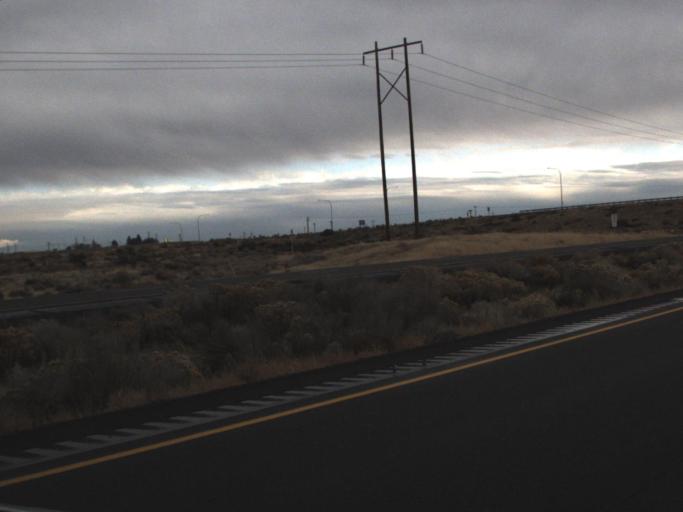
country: US
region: Washington
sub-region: Franklin County
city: Pasco
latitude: 46.2407
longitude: -119.0590
